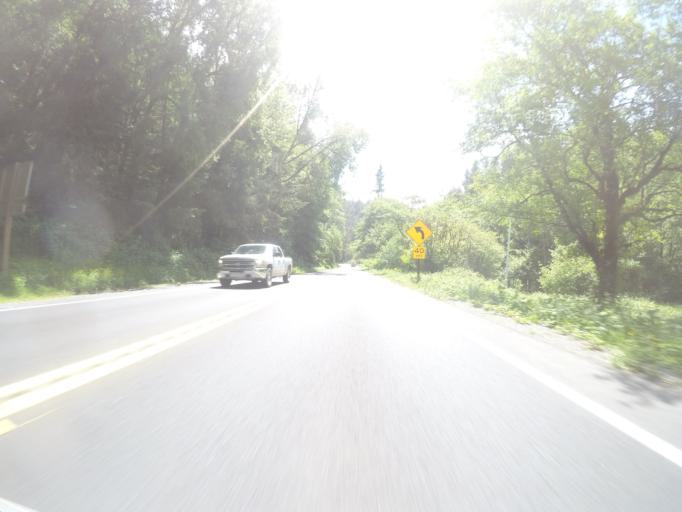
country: US
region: California
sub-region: Humboldt County
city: Westhaven-Moonstone
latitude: 41.3427
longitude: -124.0321
